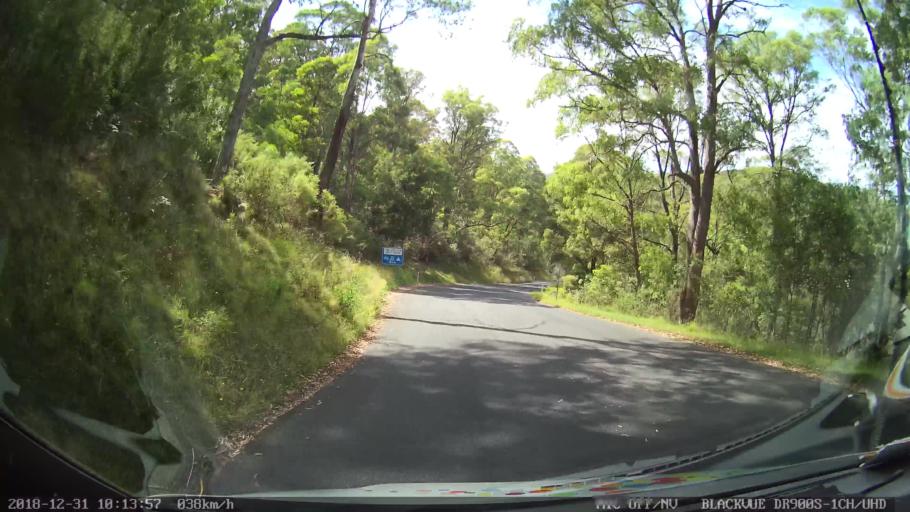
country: AU
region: New South Wales
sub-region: Snowy River
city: Jindabyne
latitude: -36.5400
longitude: 148.1523
